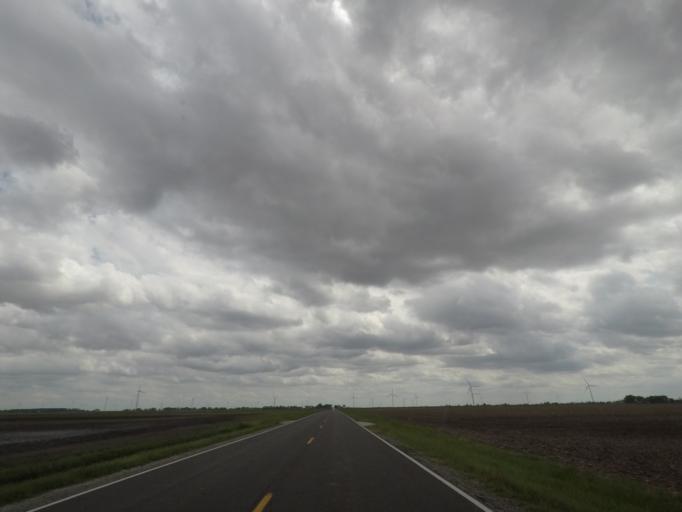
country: US
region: Illinois
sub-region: Macon County
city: Warrensburg
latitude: 40.0425
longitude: -89.0856
